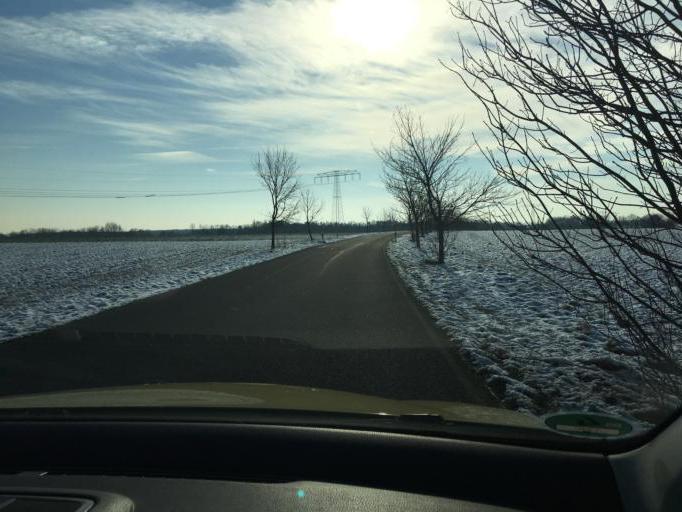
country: DE
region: Saxony
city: Belgershain
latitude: 51.2229
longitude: 12.5558
